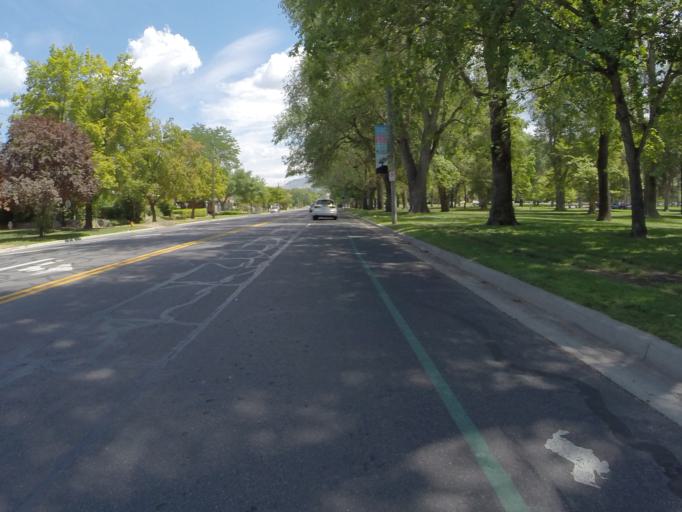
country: US
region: Utah
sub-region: Salt Lake County
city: Salt Lake City
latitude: 40.7497
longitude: -111.8736
